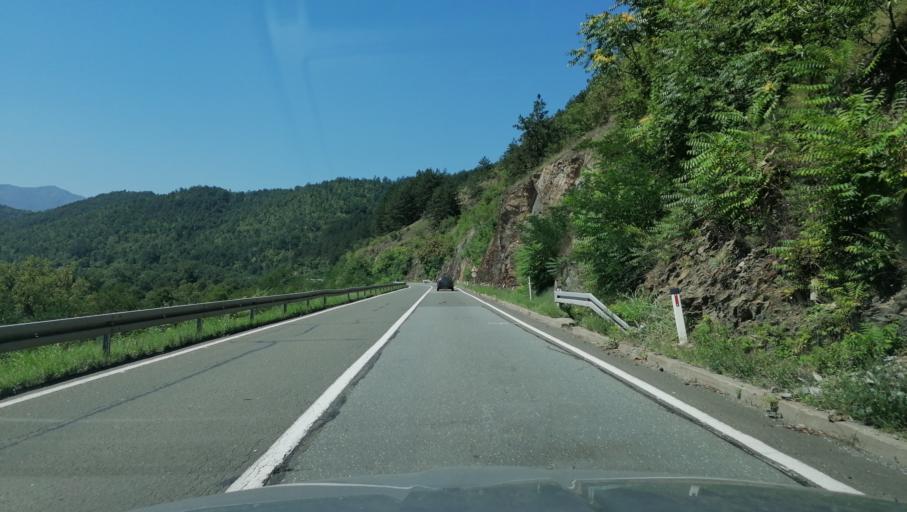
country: RS
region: Central Serbia
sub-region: Raski Okrug
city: Kraljevo
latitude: 43.6665
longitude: 20.5773
